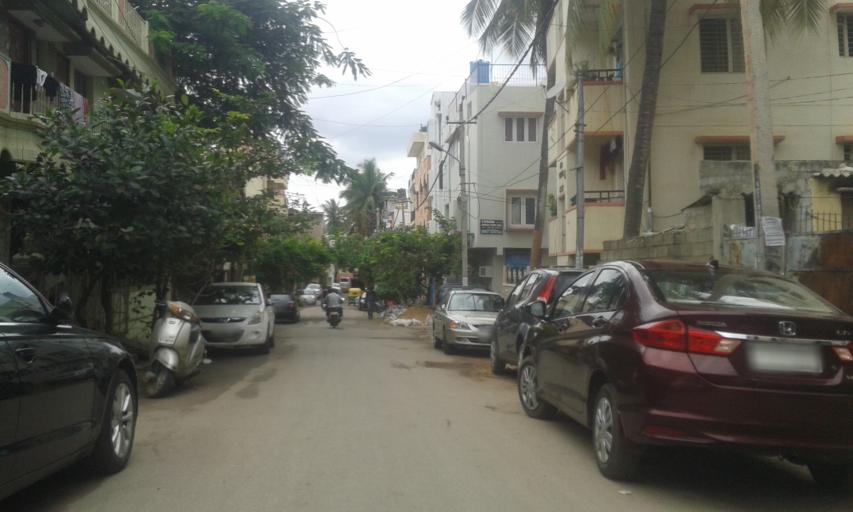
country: IN
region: Karnataka
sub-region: Bangalore Urban
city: Bangalore
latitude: 12.9620
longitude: 77.6458
